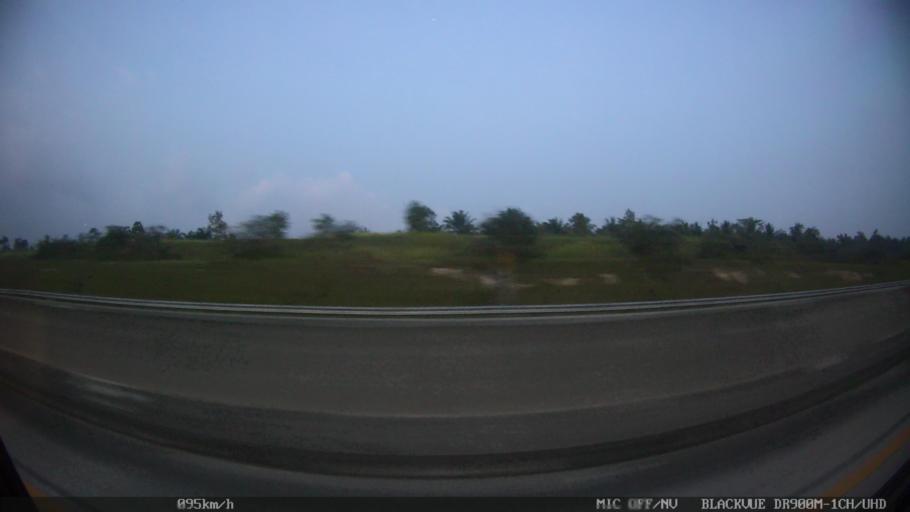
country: ID
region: Lampung
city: Sidorejo
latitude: -5.5507
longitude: 105.5248
